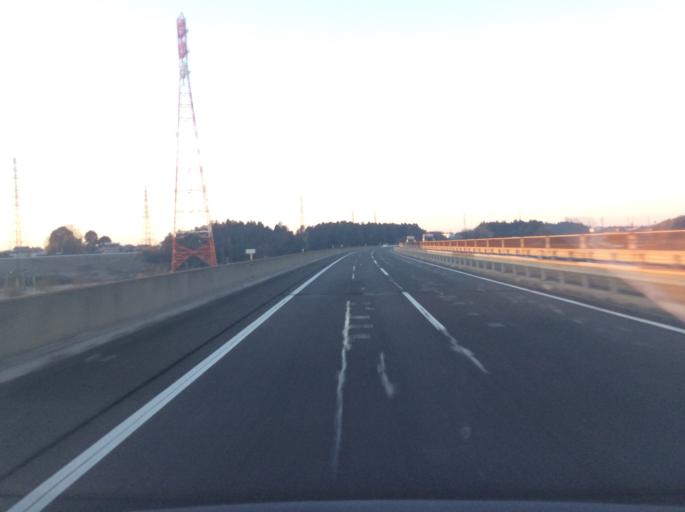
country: JP
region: Ibaraki
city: Funaishikawa
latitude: 36.4948
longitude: 140.5642
